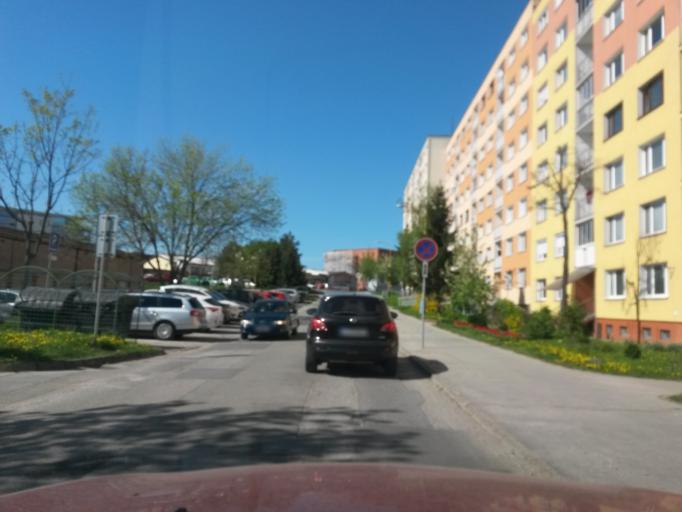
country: SK
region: Kosicky
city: Kosice
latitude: 48.7072
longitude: 21.2494
